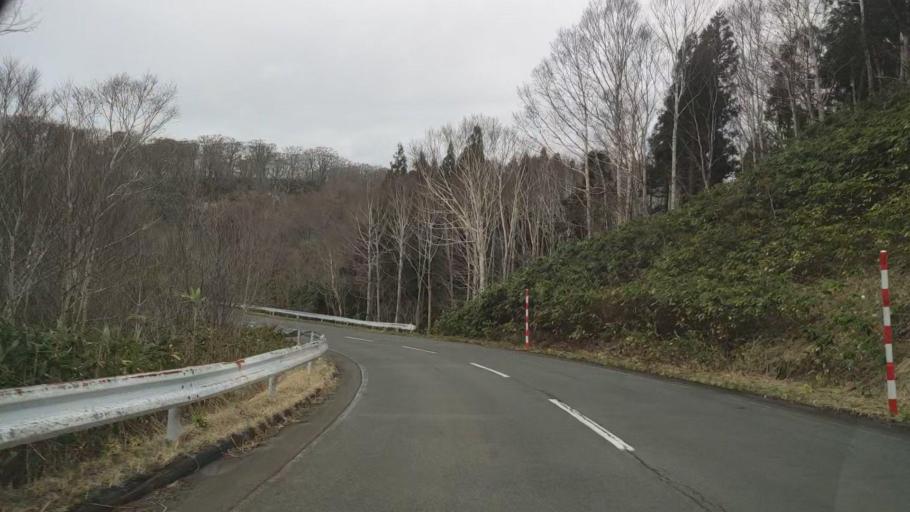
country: JP
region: Akita
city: Hanawa
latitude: 40.4174
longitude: 140.8405
